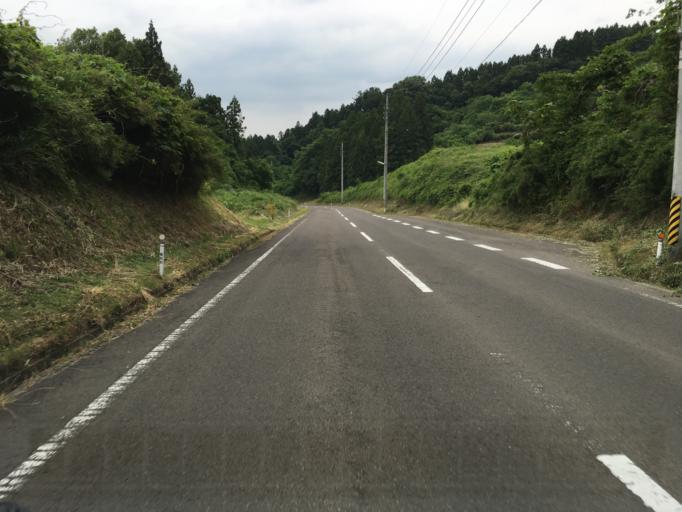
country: JP
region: Fukushima
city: Nihommatsu
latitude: 37.6219
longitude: 140.5243
